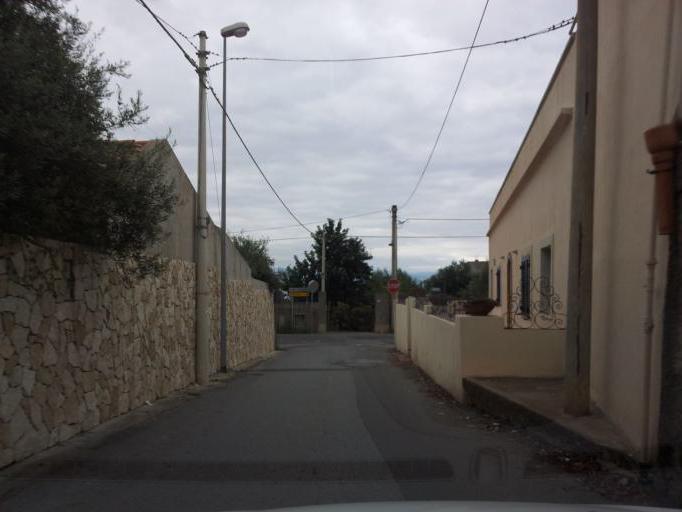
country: IT
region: Sicily
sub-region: Messina
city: Milazzo
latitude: 38.2485
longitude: 15.2449
